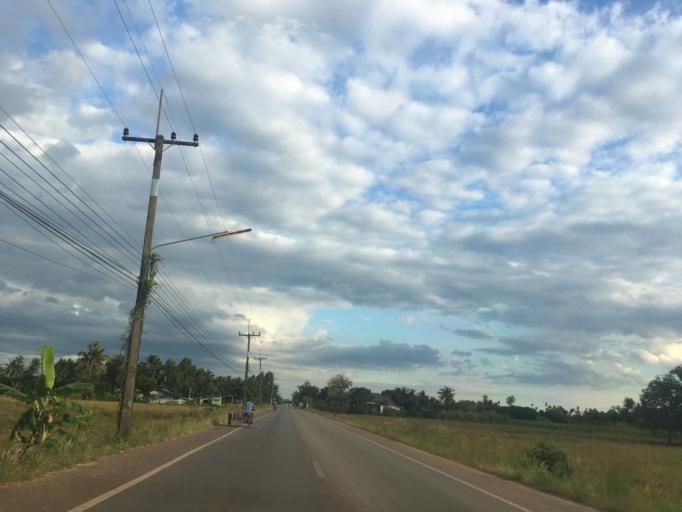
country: TH
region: Chanthaburi
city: Na Yai Am
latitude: 12.7256
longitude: 101.7554
